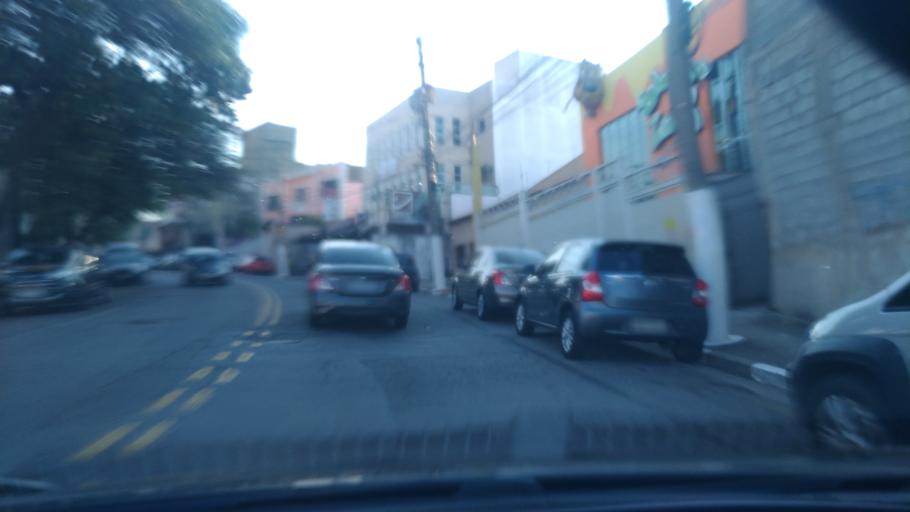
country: BR
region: Sao Paulo
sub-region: Osasco
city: Osasco
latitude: -23.5340
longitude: -46.7908
